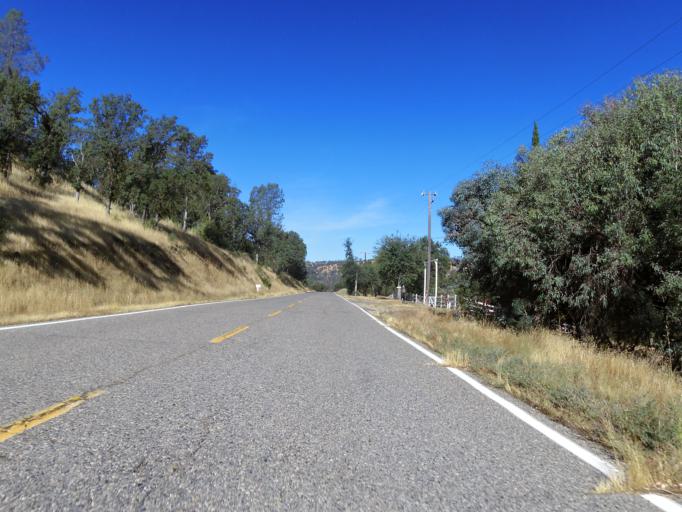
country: US
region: California
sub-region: Madera County
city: Yosemite Lakes
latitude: 37.2102
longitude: -119.7934
